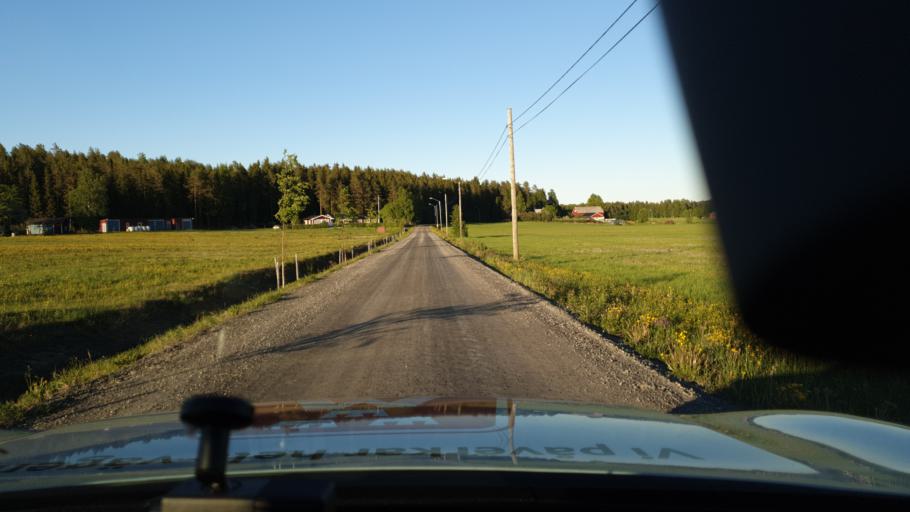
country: SE
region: Vaesterbotten
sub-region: Umea Kommun
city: Roback
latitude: 64.0070
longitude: 20.0584
